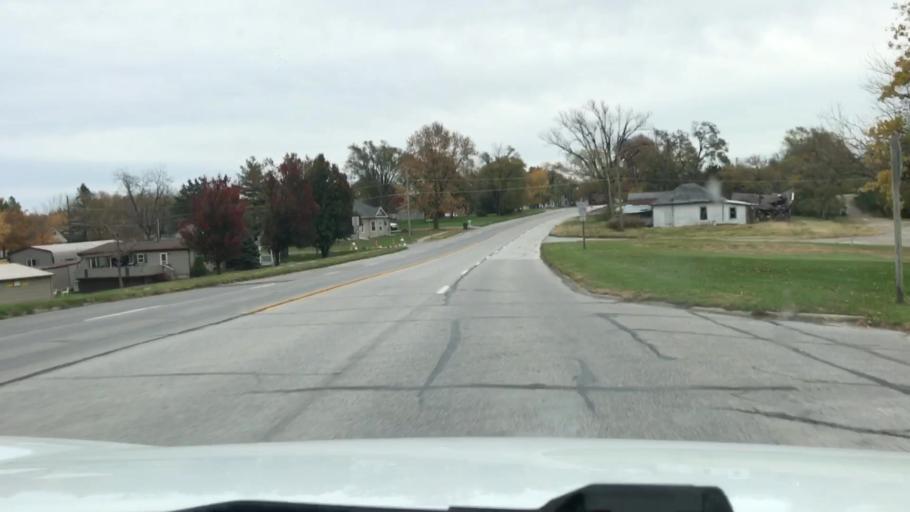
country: US
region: Iowa
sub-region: Lee County
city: Keokuk
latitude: 40.3897
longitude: -91.4122
